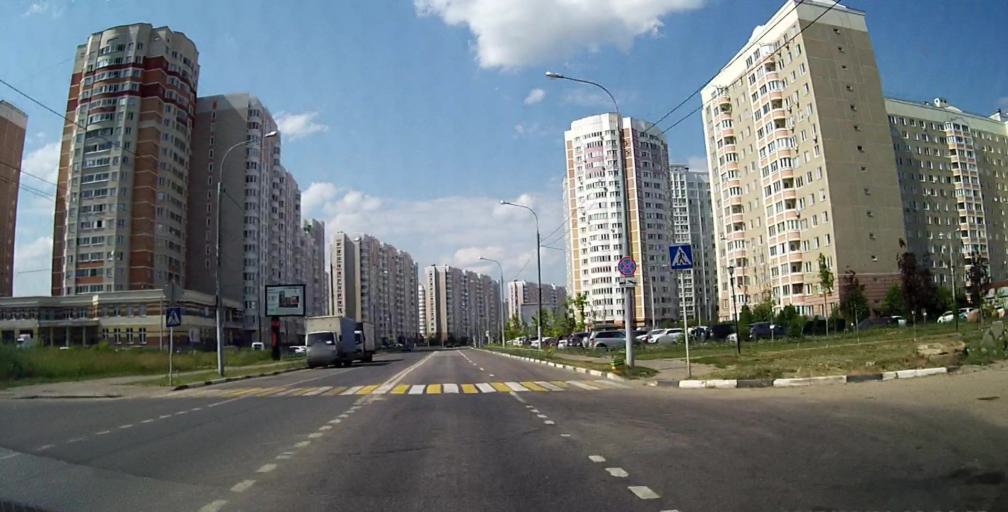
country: RU
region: Moskovskaya
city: Dubrovitsy
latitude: 55.4126
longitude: 37.4823
